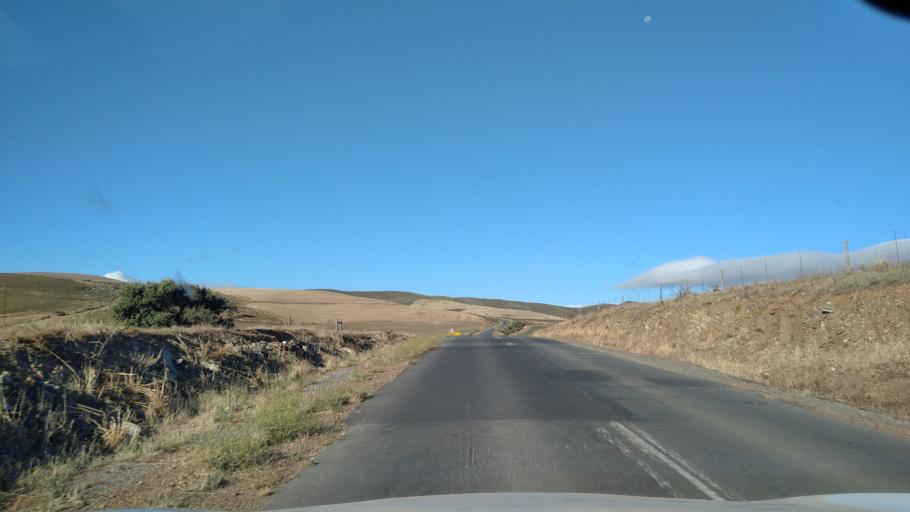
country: ZA
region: Western Cape
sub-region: Overberg District Municipality
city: Caledon
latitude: -34.1637
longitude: 19.3000
